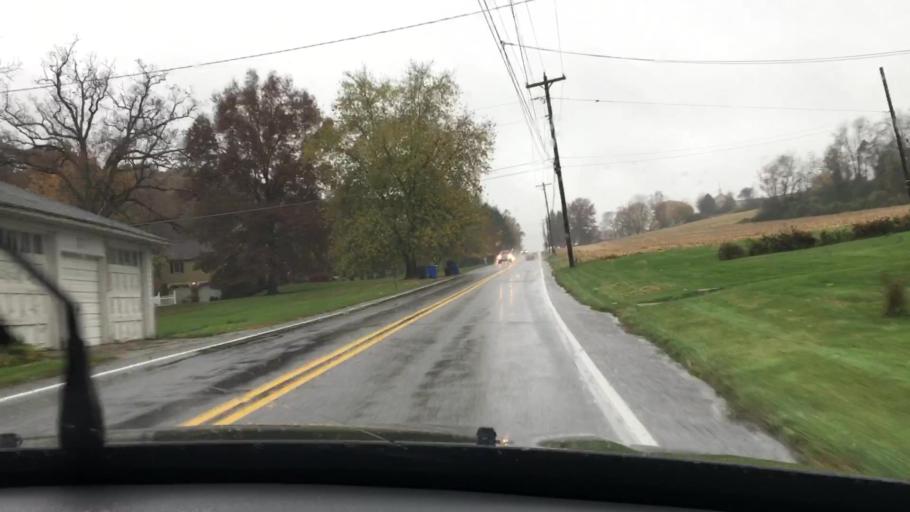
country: US
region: Pennsylvania
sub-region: York County
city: Glen Rock
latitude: 39.7657
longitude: -76.7624
